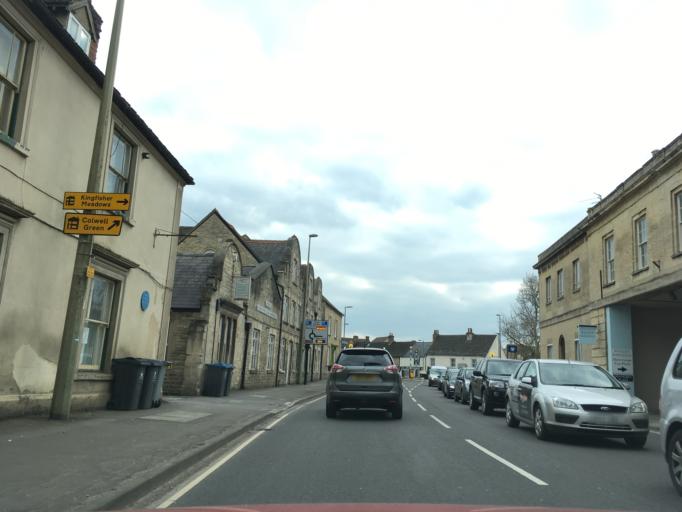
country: GB
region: England
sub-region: Oxfordshire
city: Witney
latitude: 51.7898
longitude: -1.4821
